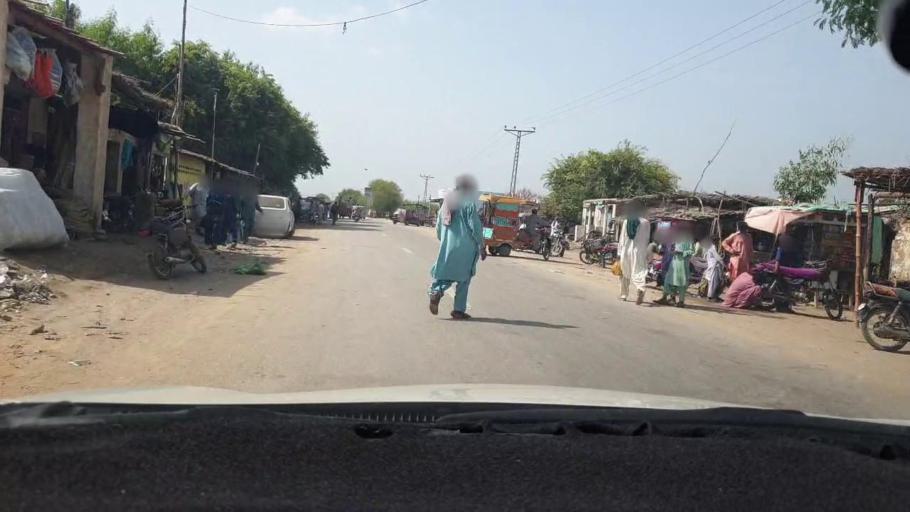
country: PK
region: Sindh
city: Mirpur Khas
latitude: 25.7083
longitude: 69.1281
